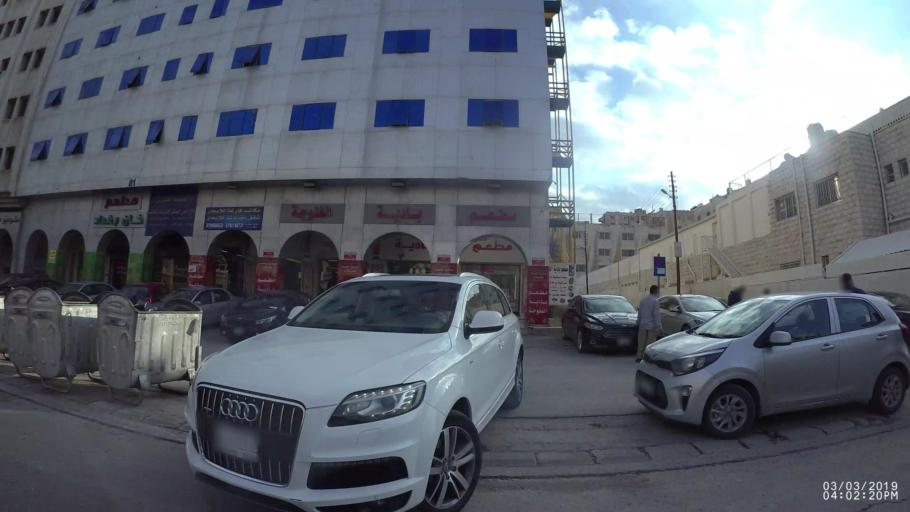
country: JO
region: Amman
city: Al Jubayhah
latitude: 31.9856
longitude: 35.8806
